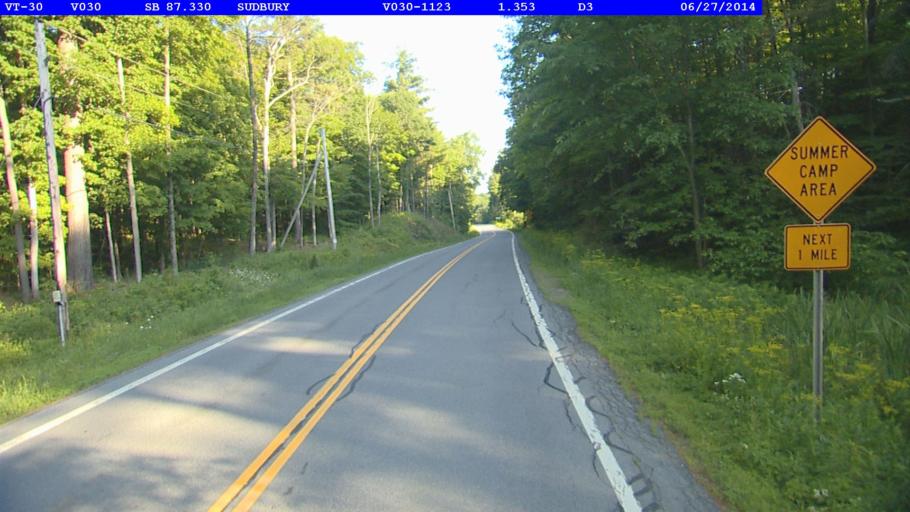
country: US
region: Vermont
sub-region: Rutland County
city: Brandon
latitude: 43.7685
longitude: -73.1979
